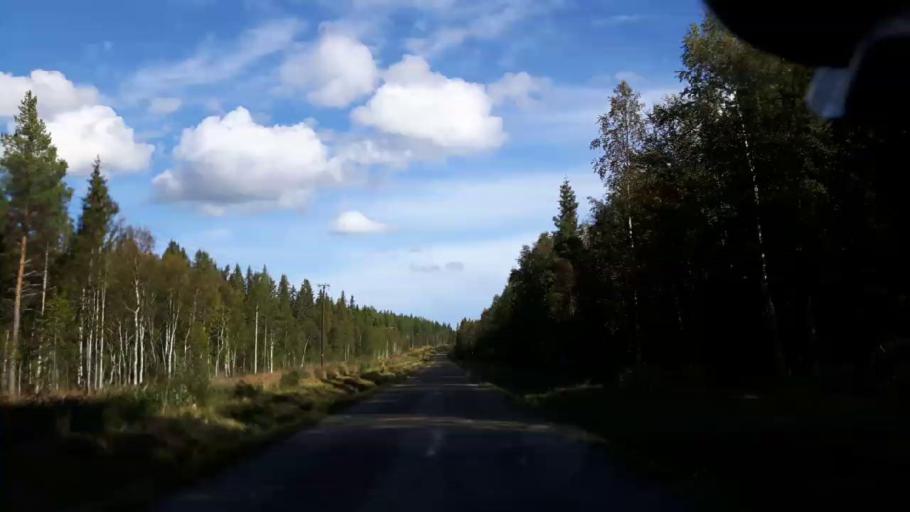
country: SE
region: Jaemtland
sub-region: Ragunda Kommun
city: Hammarstrand
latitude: 63.4354
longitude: 16.0240
